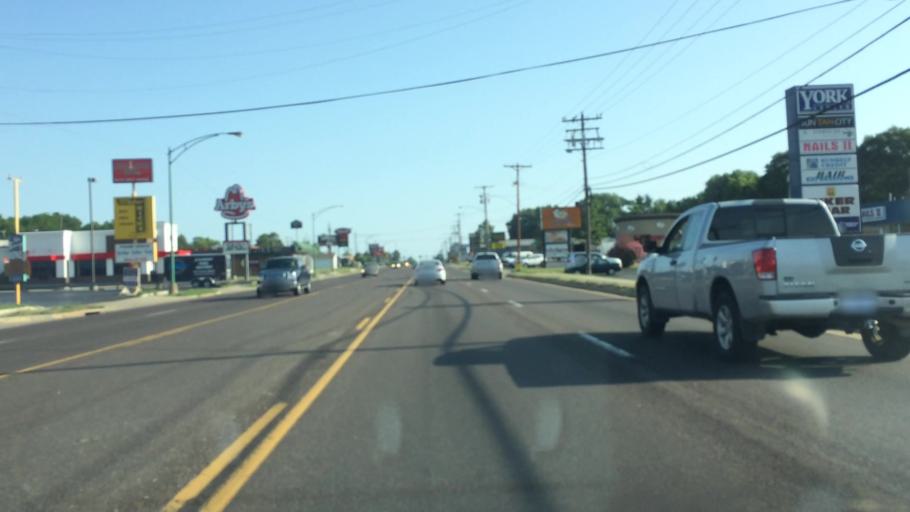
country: US
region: Missouri
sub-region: Greene County
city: Springfield
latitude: 37.1734
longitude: -93.2953
